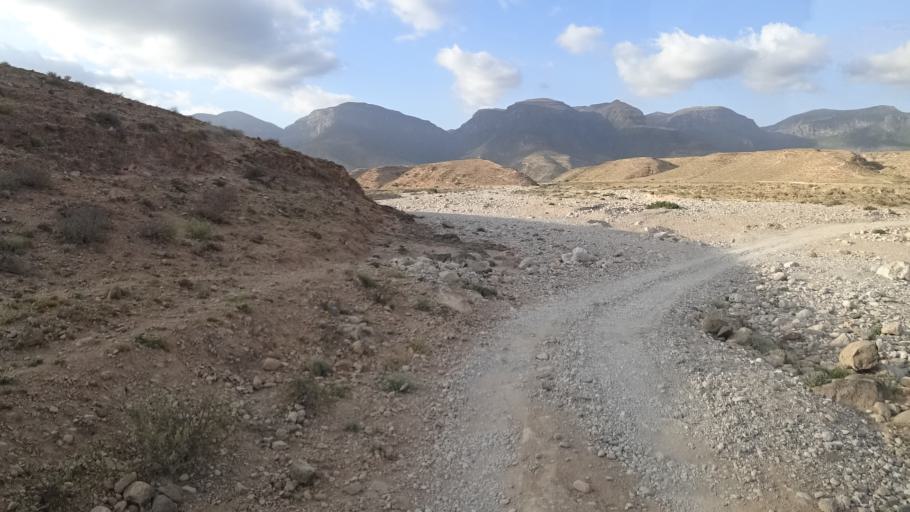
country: OM
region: Zufar
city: Salalah
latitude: 16.9768
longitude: 53.8523
